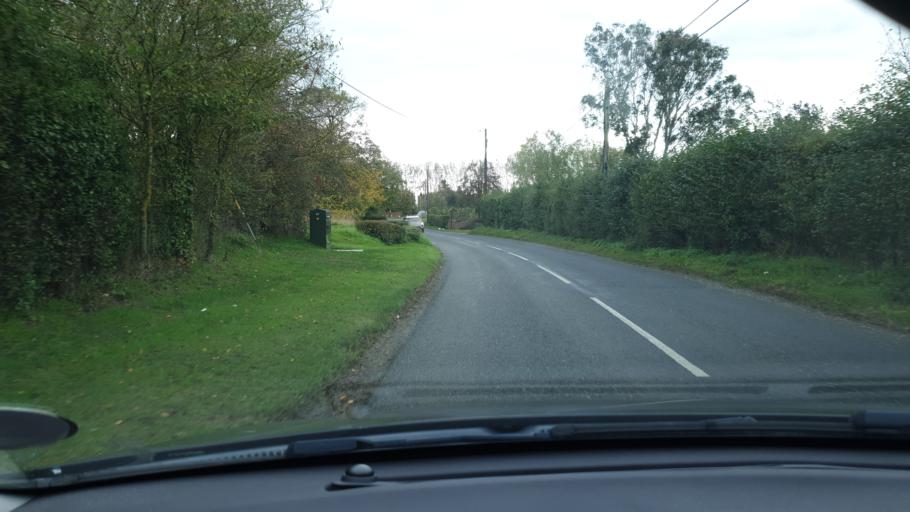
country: GB
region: England
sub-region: Essex
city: Manningtree
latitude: 51.9311
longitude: 1.0484
